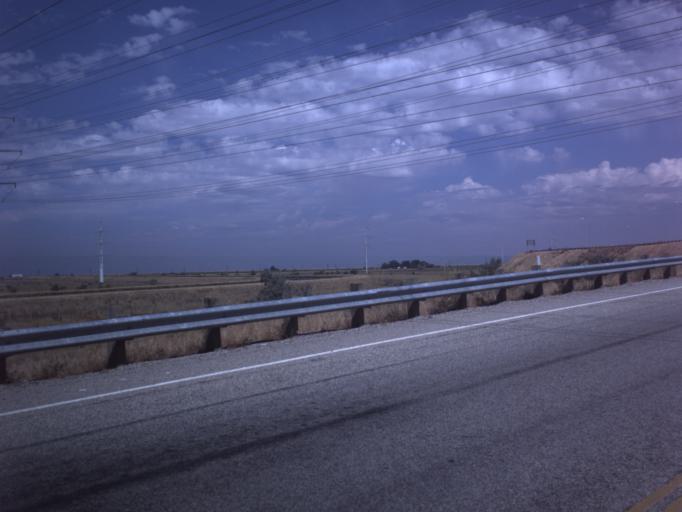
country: US
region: Utah
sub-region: Box Elder County
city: South Willard
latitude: 41.3378
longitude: -112.0376
